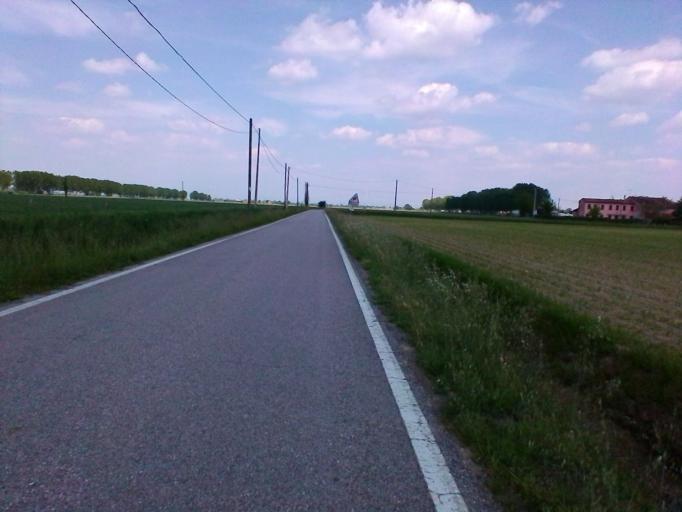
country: IT
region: Lombardy
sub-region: Provincia di Mantova
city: Sant'Antonio
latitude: 45.2291
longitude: 10.8249
